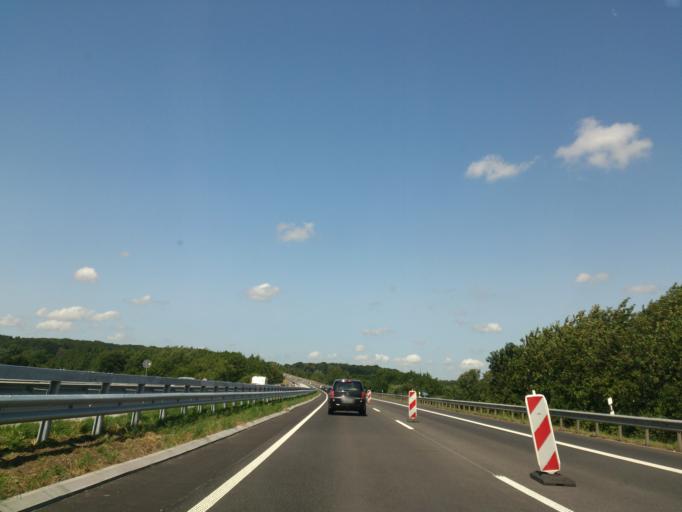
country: DE
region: Schleswig-Holstein
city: Arkebek
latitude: 54.1420
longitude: 9.2477
